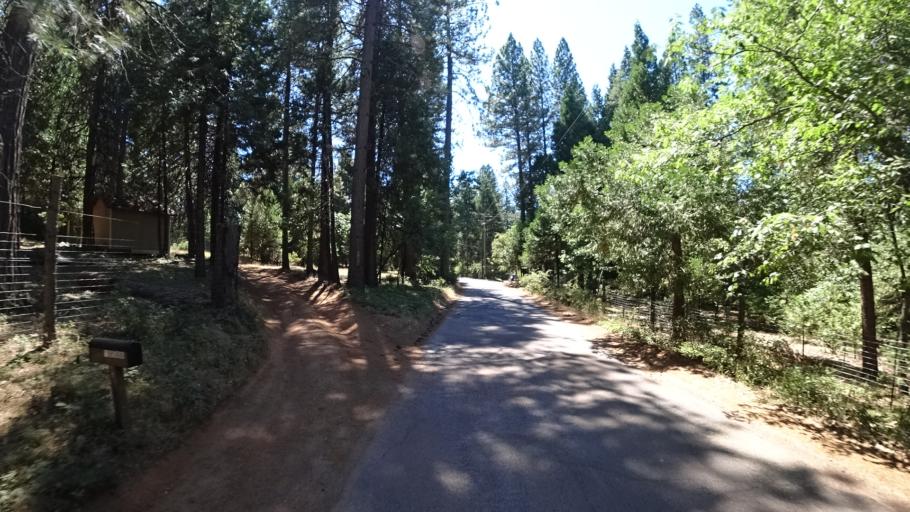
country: US
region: California
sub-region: Calaveras County
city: Mountain Ranch
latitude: 38.2810
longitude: -120.5416
